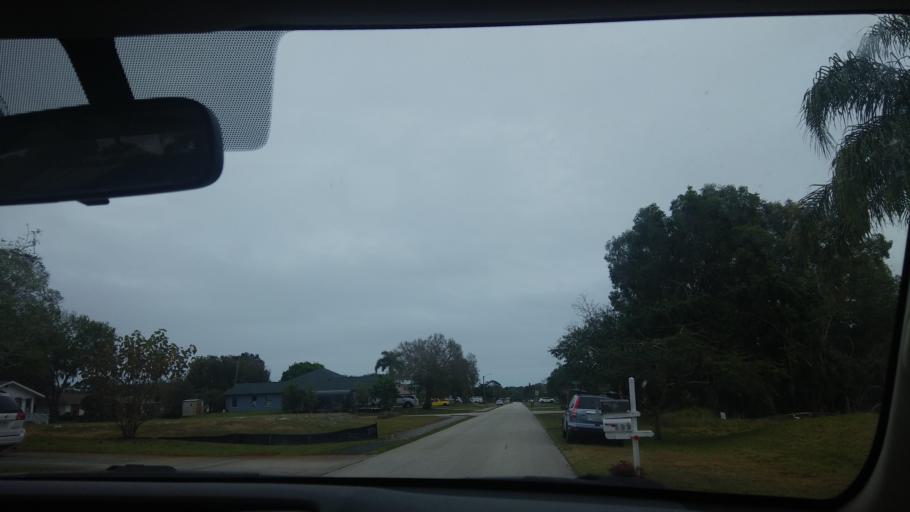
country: US
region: Florida
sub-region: Indian River County
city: Sebastian
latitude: 27.8000
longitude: -80.4863
